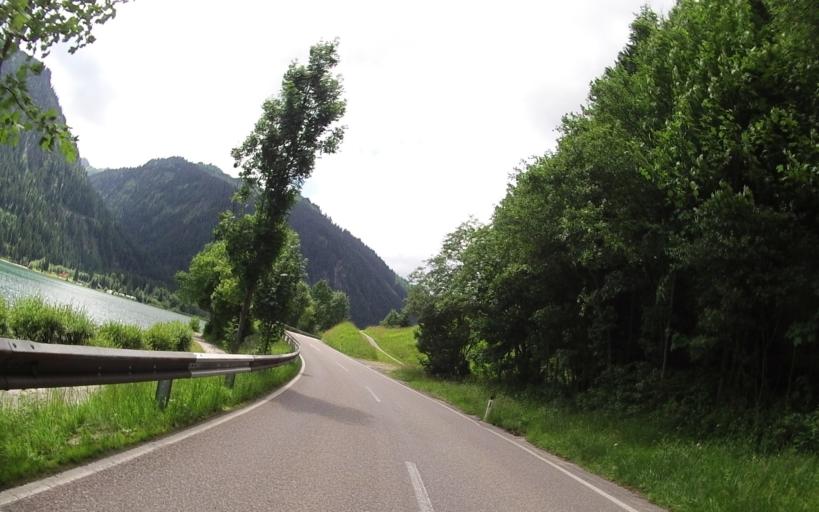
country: AT
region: Tyrol
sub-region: Politischer Bezirk Reutte
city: Graen
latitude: 47.4942
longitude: 10.5752
